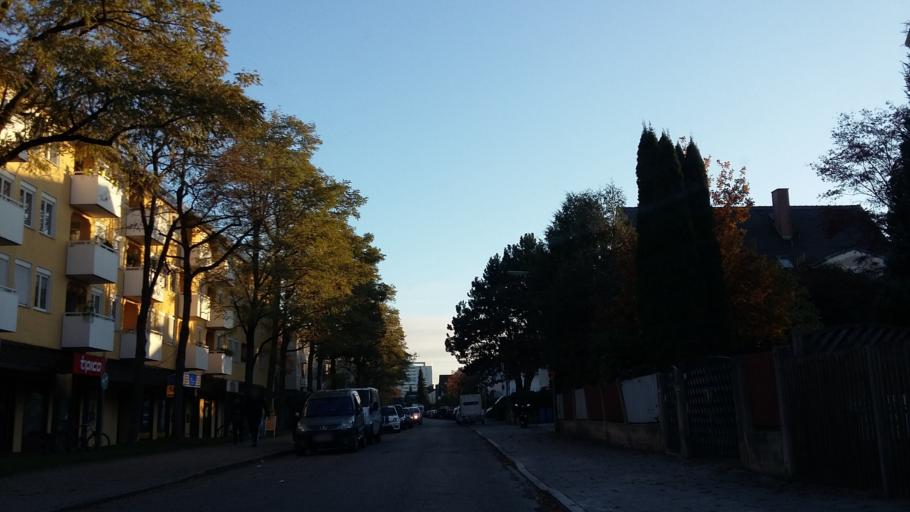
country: DE
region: Bavaria
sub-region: Upper Bavaria
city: Pasing
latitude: 48.1298
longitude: 11.4895
